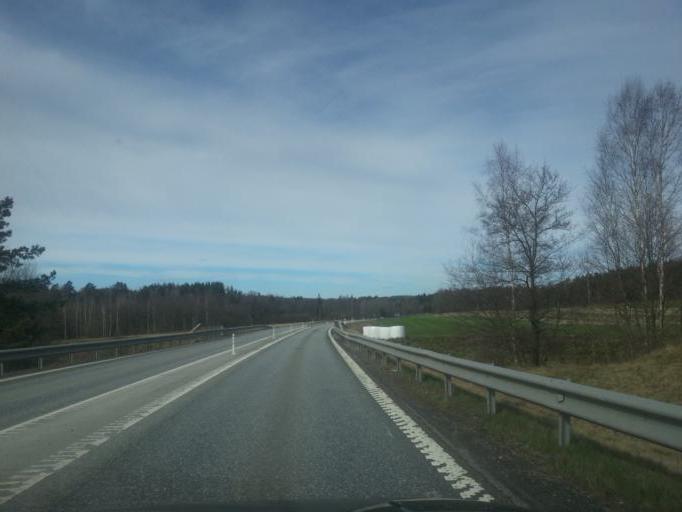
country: SE
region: Joenkoeping
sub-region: Jonkopings Kommun
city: Bankeryd
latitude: 57.8579
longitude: 14.1036
